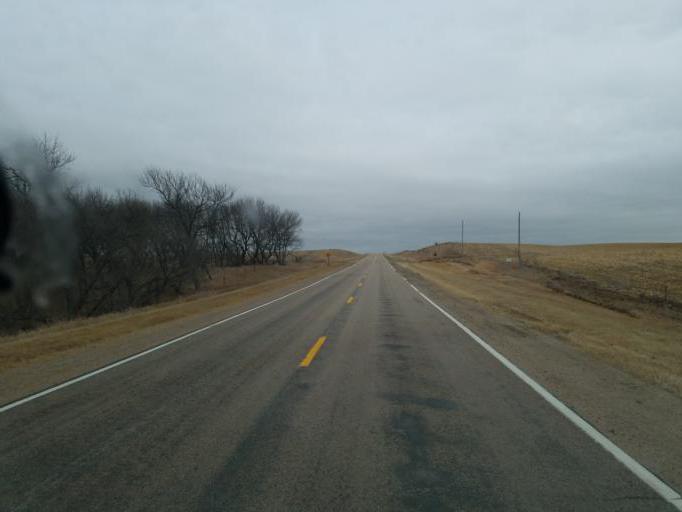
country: US
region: Nebraska
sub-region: Knox County
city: Bloomfield
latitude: 42.6127
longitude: -97.4925
